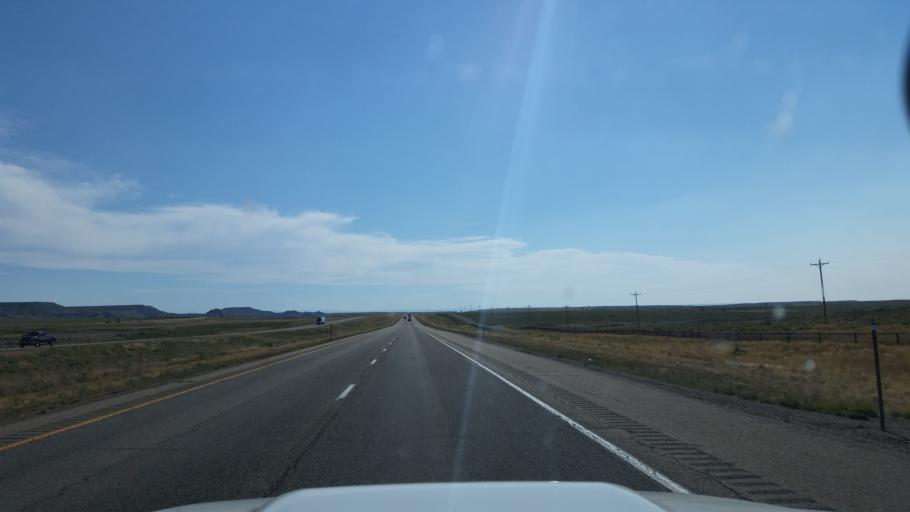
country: US
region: Wyoming
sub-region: Uinta County
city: Lyman
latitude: 41.4530
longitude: -110.0702
